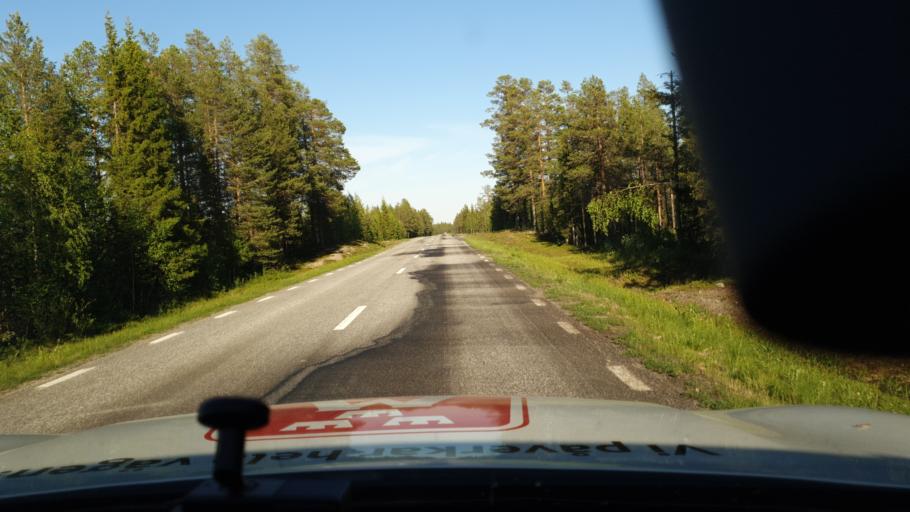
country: SE
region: Vaesterbotten
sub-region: Lycksele Kommun
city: Soderfors
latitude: 64.6245
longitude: 18.0911
